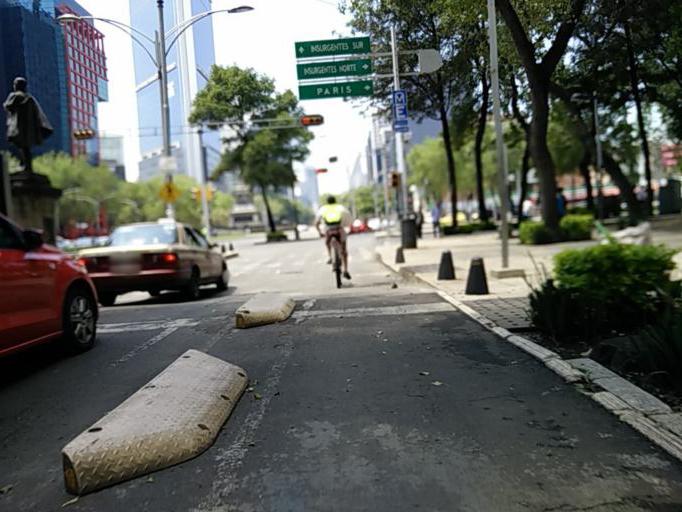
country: MX
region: Mexico City
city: Cuauhtemoc
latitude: 19.4317
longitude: -99.1581
